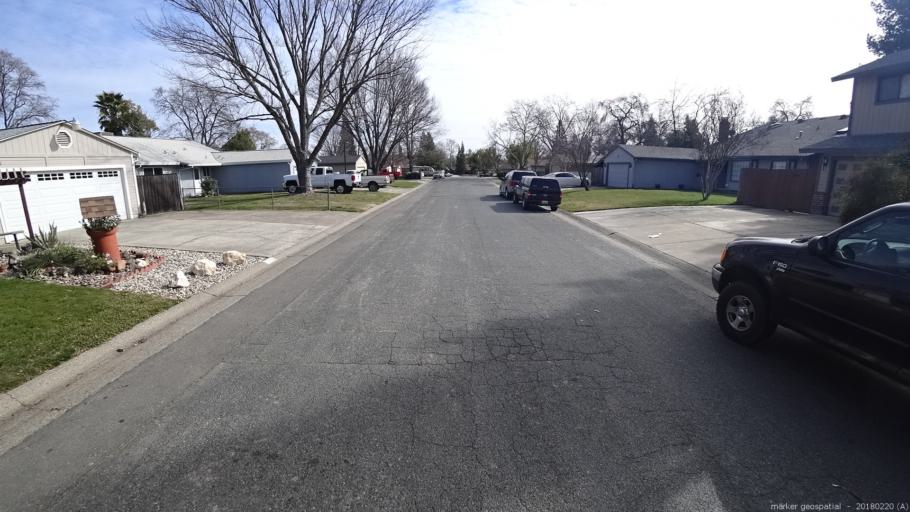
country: US
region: California
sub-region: Sacramento County
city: Orangevale
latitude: 38.6754
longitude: -121.2286
